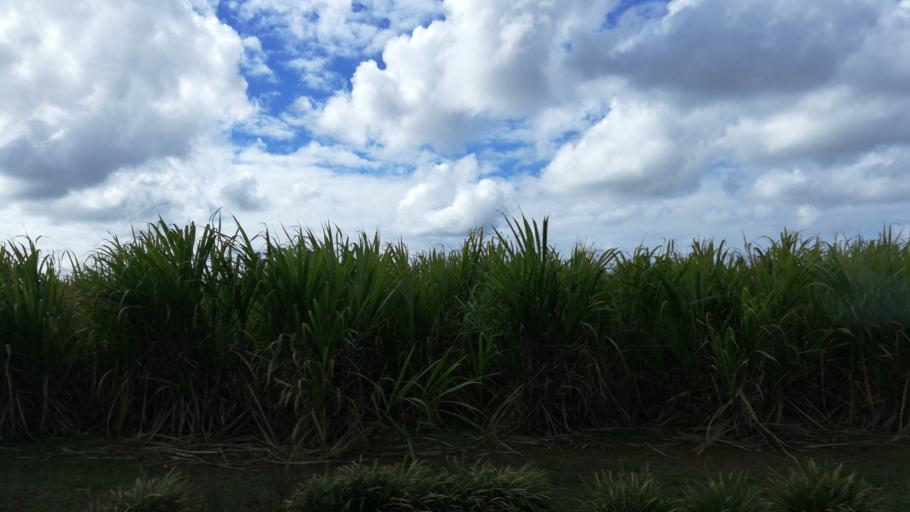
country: MU
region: Flacq
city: Camp de Masque
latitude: -20.2174
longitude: 57.6745
